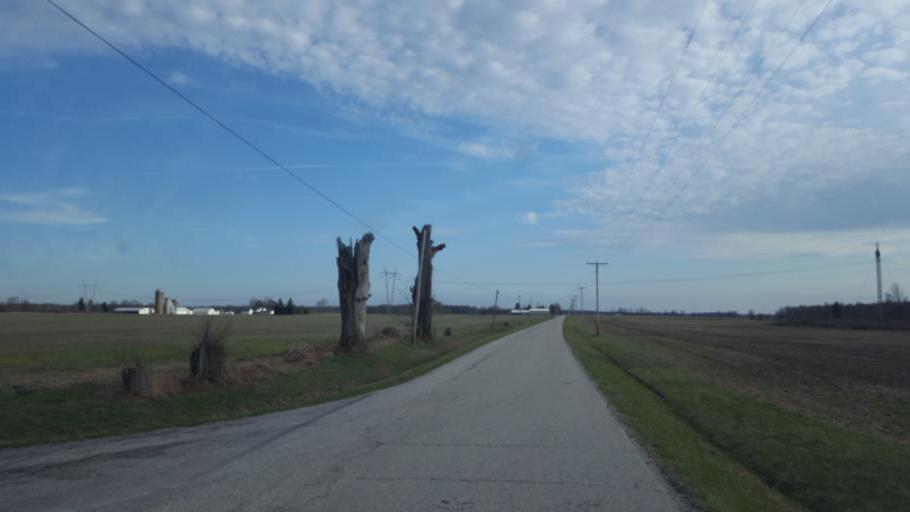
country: US
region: Ohio
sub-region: Crawford County
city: Bucyrus
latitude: 40.7473
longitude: -82.9376
